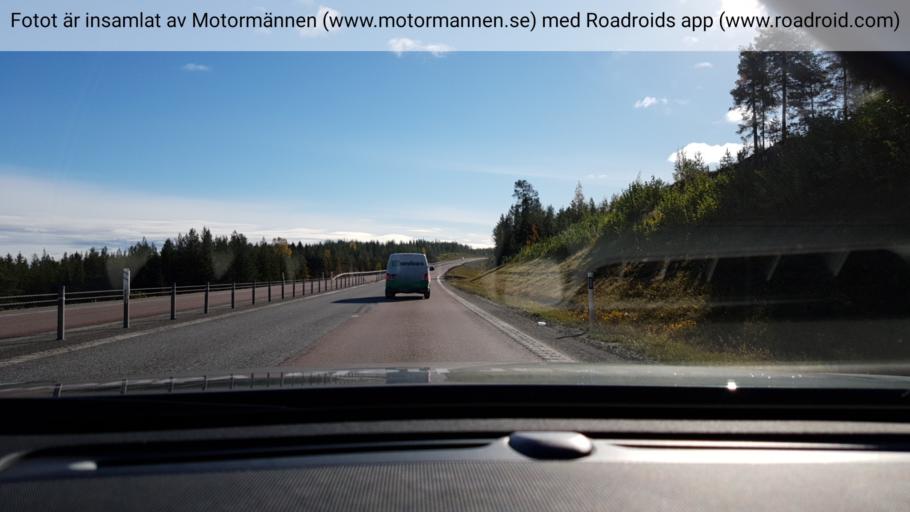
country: SE
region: Vaesterbotten
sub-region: Skelleftea Kommun
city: Soedra Bergsbyn
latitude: 64.6860
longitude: 21.0579
